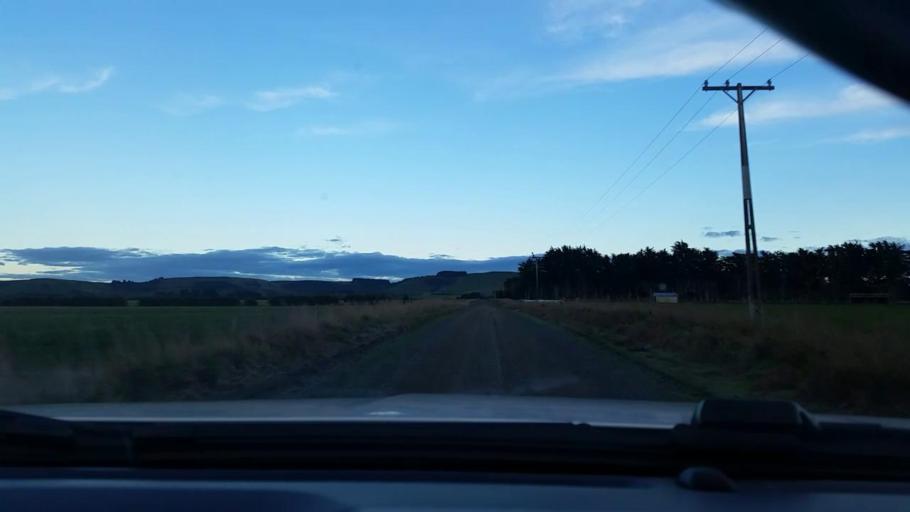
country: NZ
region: Southland
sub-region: Southland District
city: Winton
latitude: -46.1075
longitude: 168.4458
